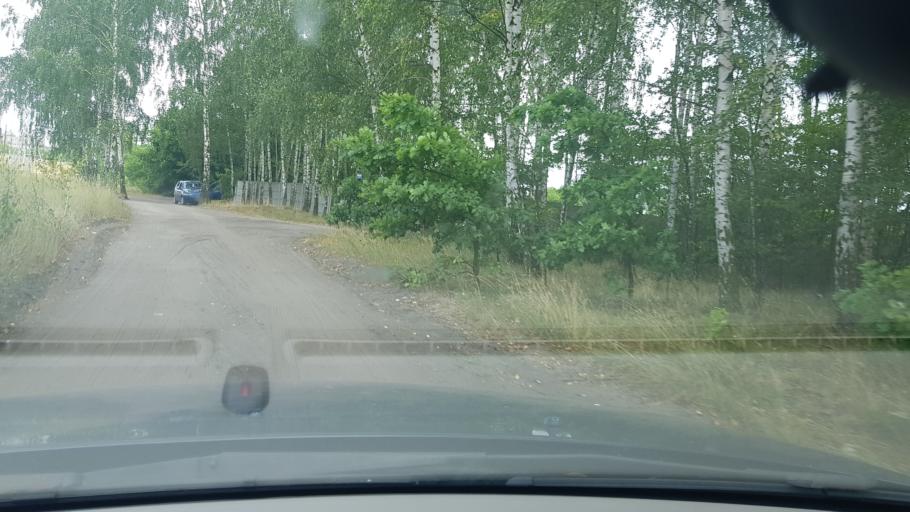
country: PL
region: Lodz Voivodeship
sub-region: Powiat tomaszowski
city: Tomaszow Mazowiecki
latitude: 51.5527
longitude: 20.0237
